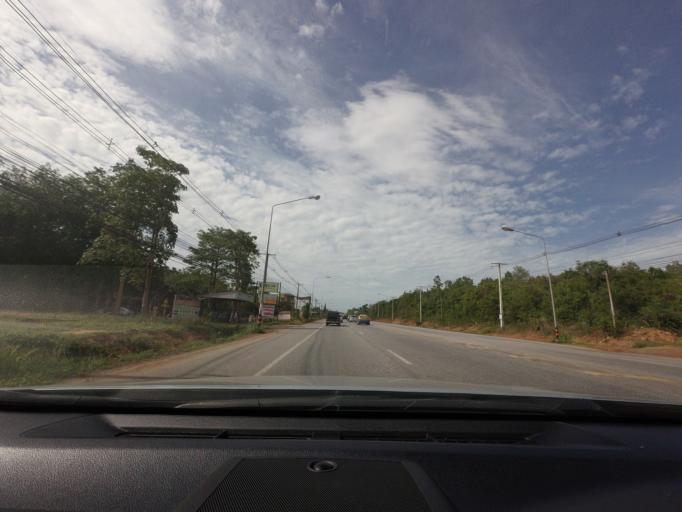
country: TH
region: Songkhla
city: Hat Yai
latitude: 6.9632
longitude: 100.4254
